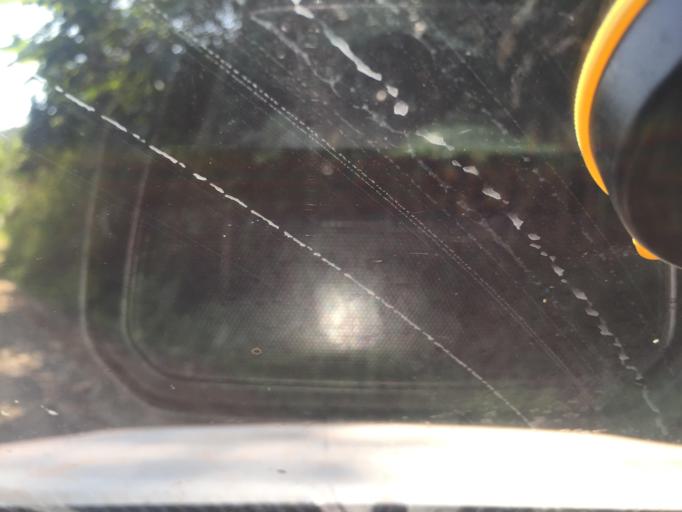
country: LA
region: Phongsali
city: Phongsali
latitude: 21.6566
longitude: 102.4144
